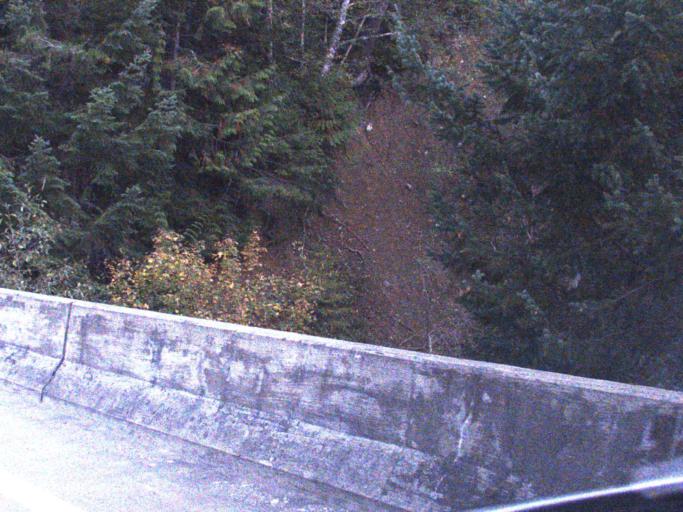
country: US
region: Washington
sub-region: Snohomish County
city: Darrington
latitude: 48.7071
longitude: -120.9764
